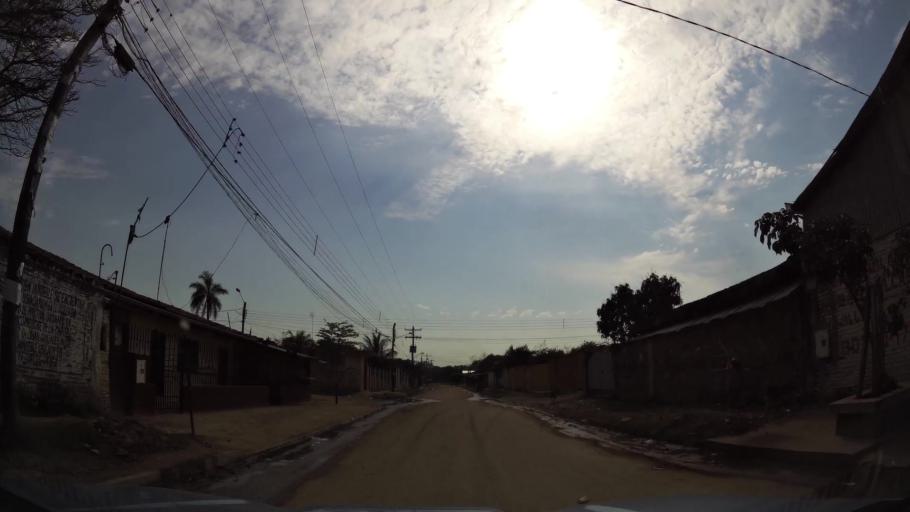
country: BO
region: Santa Cruz
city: Santa Cruz de la Sierra
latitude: -17.7211
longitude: -63.1361
